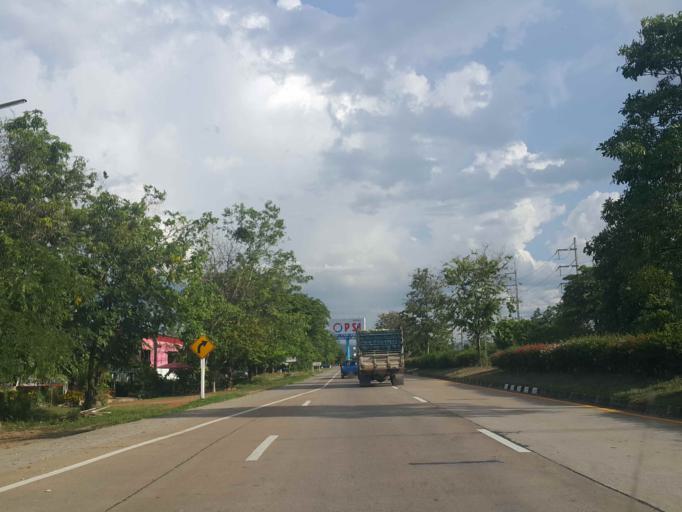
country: TH
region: Phrae
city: Sung Men
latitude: 18.0278
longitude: 100.1110
